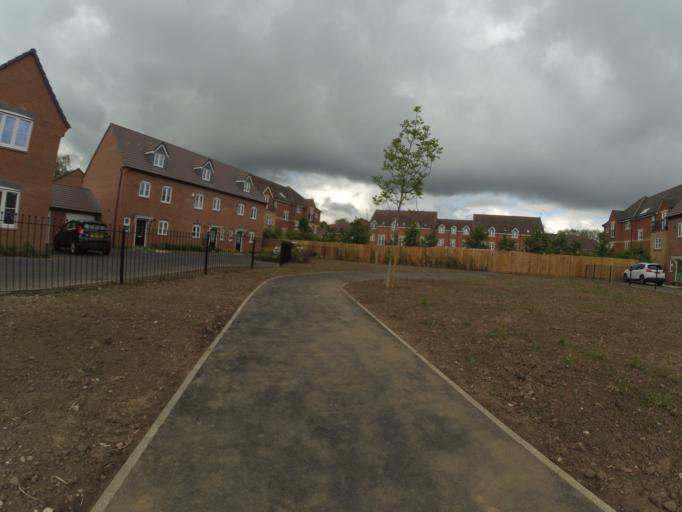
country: GB
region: England
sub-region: Warwickshire
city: Rugby
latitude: 52.3702
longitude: -1.2445
